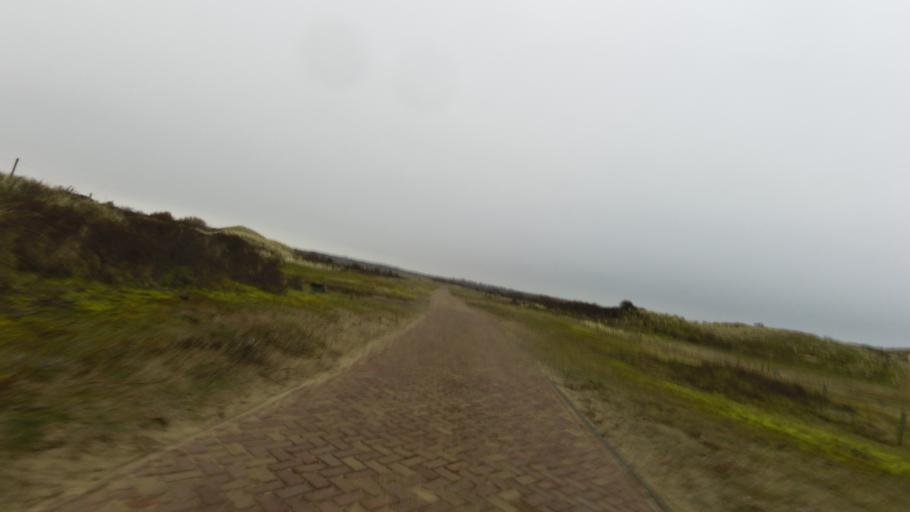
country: NL
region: North Holland
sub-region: Gemeente Castricum
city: Castricum
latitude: 52.5469
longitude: 4.6107
